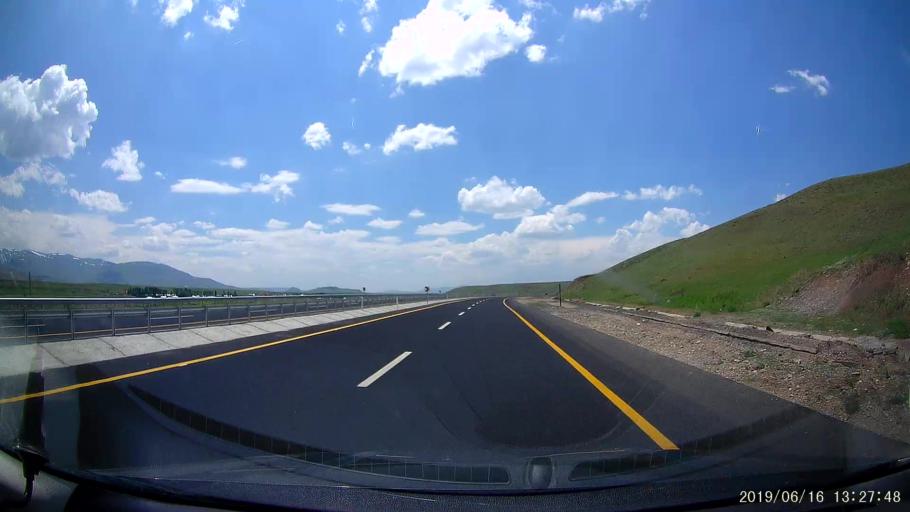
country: TR
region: Agri
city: Murat
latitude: 39.6713
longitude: 43.3015
